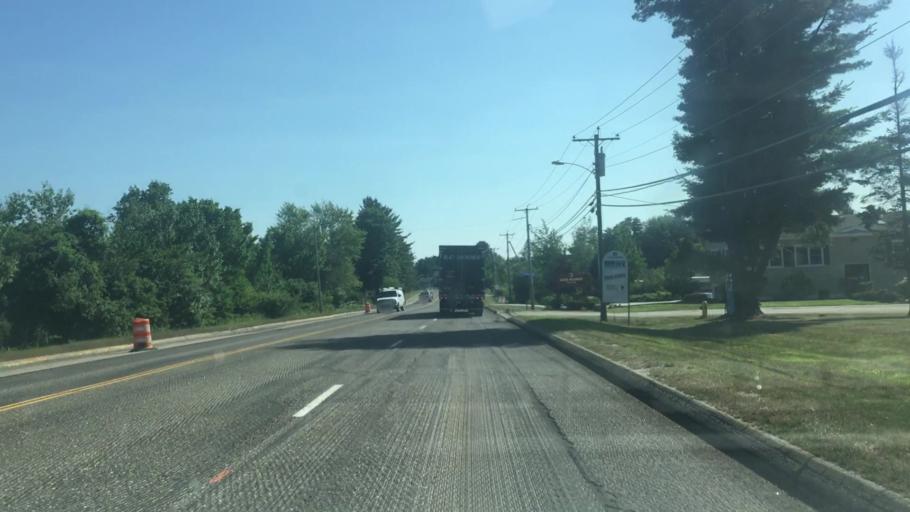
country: US
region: Maine
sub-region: York County
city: Saco
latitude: 43.5190
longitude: -70.4504
